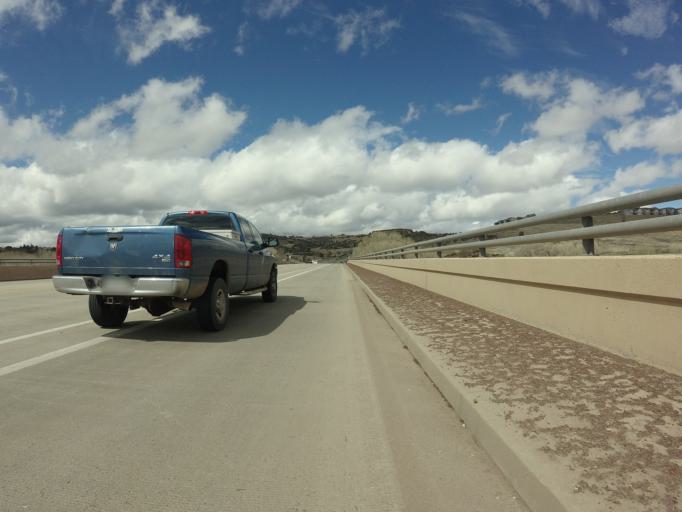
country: US
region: Arizona
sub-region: Yavapai County
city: Prescott
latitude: 34.5759
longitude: -112.4303
